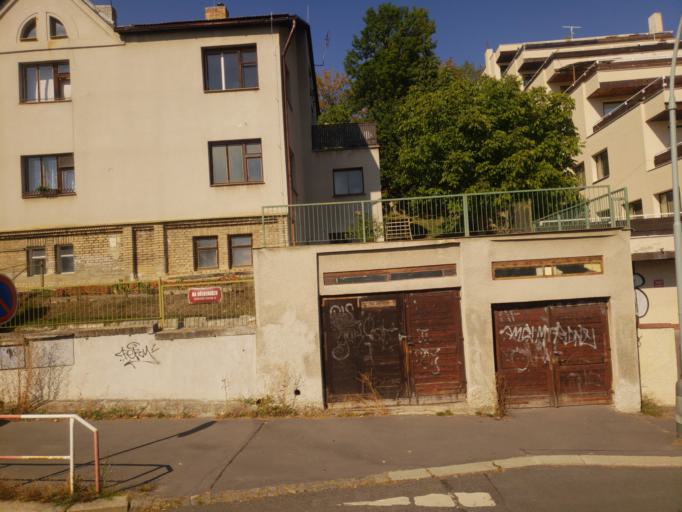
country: CZ
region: Praha
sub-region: Praha 1
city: Mala Strana
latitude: 50.0772
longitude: 14.3876
